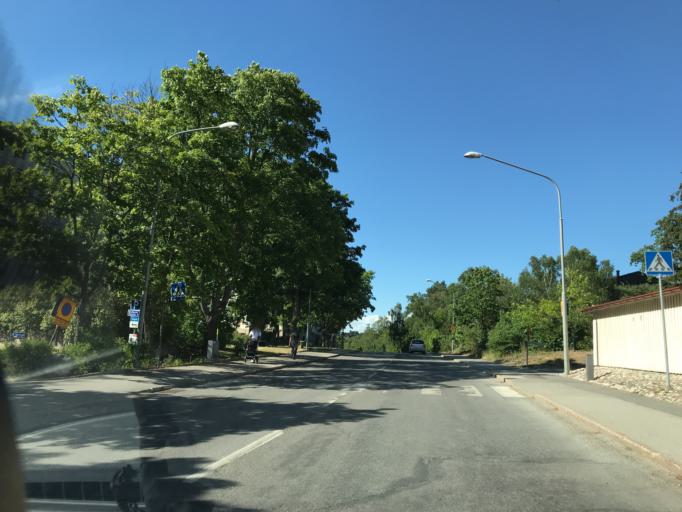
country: SE
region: Stockholm
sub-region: Huddinge Kommun
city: Segeltorp
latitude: 59.2972
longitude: 17.9424
